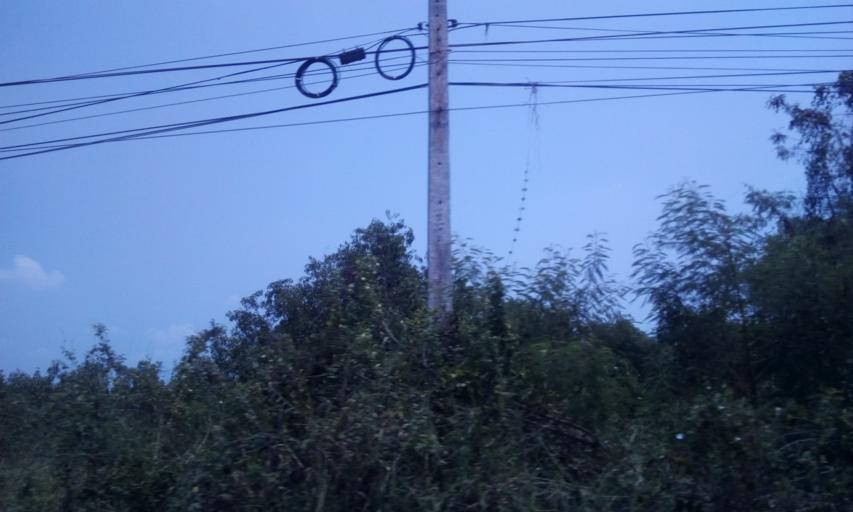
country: TH
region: Chachoengsao
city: Bang Nam Priao
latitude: 13.7688
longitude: 101.0682
